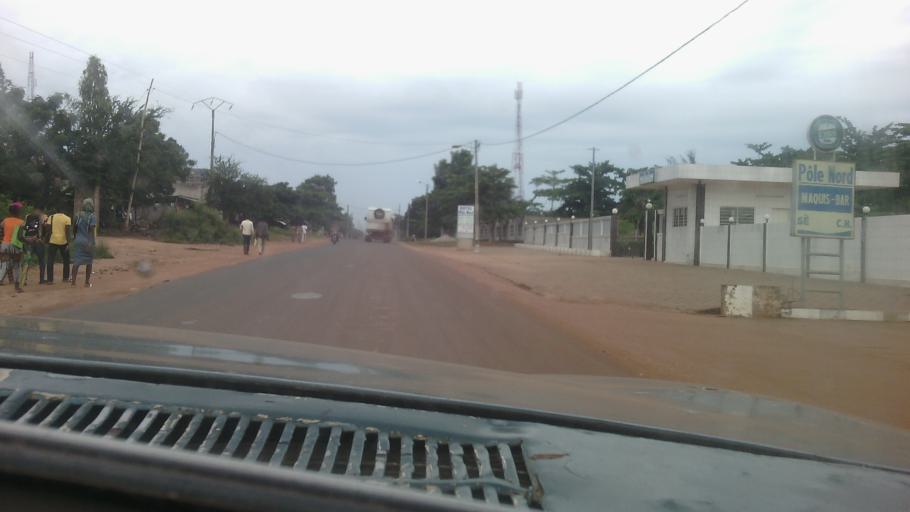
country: BJ
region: Mono
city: Come
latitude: 6.5209
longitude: 1.8206
